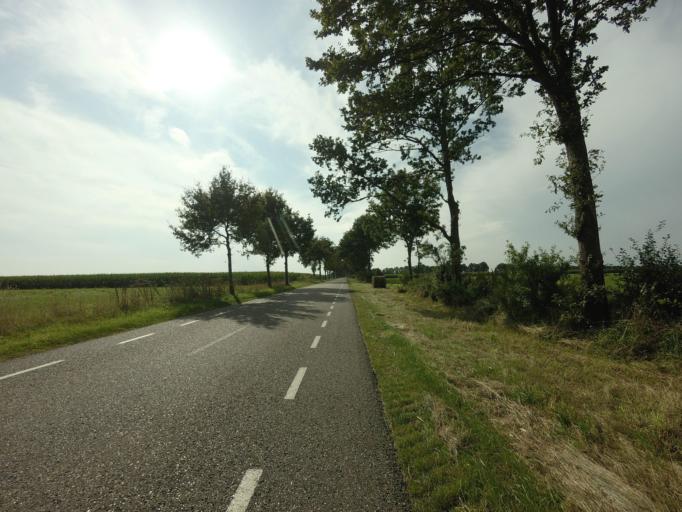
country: NL
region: Drenthe
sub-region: Gemeente Coevorden
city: Dalen
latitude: 52.6941
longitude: 6.7270
